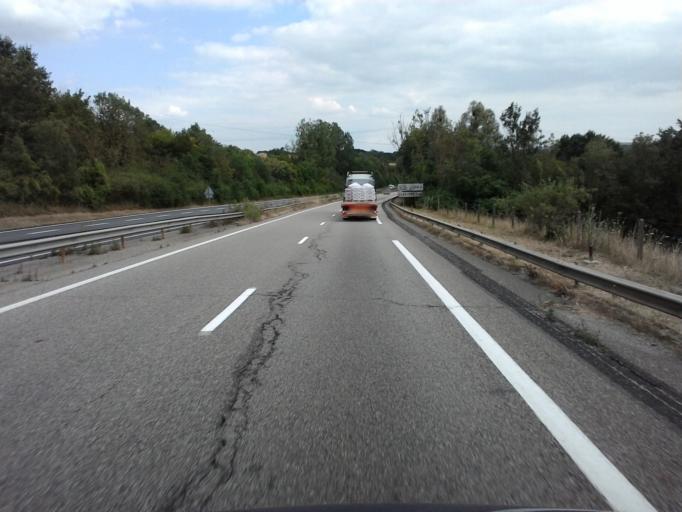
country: FR
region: Lorraine
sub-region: Departement de Meurthe-et-Moselle
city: Richardmenil
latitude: 48.5884
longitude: 6.1750
